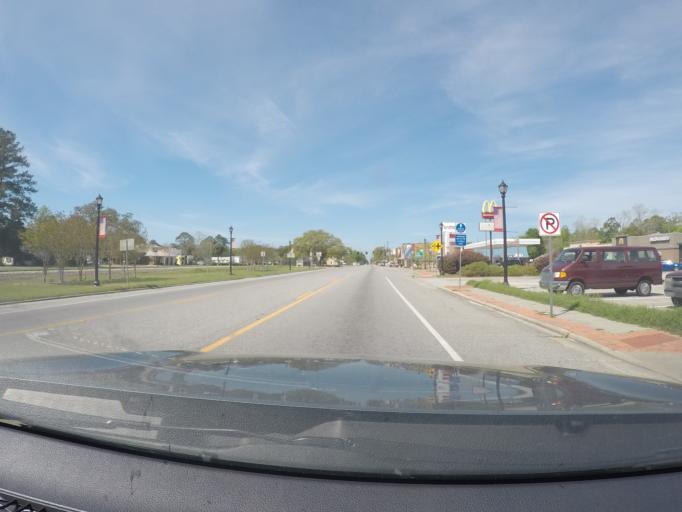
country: US
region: Georgia
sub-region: Bryan County
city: Pembroke
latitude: 32.1357
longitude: -81.6206
